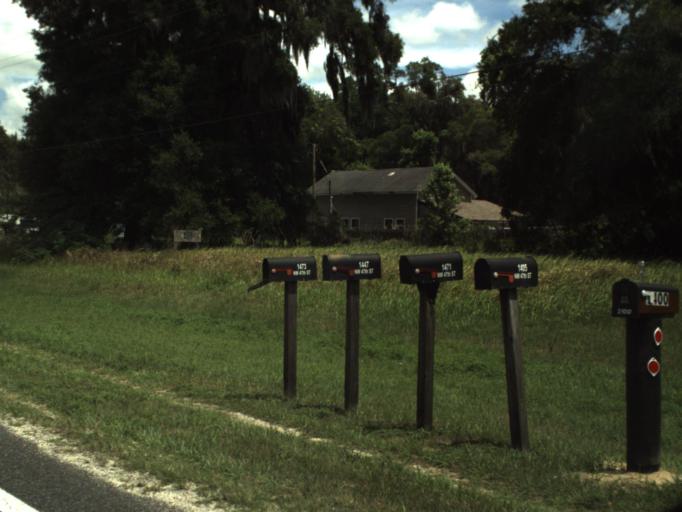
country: US
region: Florida
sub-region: Marion County
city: Ocala
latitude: 29.2359
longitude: -82.1513
